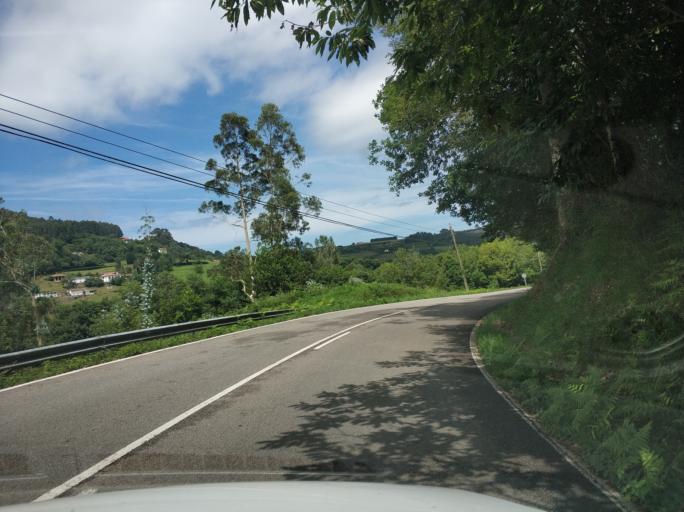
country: ES
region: Asturias
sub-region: Province of Asturias
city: Cudillero
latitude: 43.5541
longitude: -6.2291
